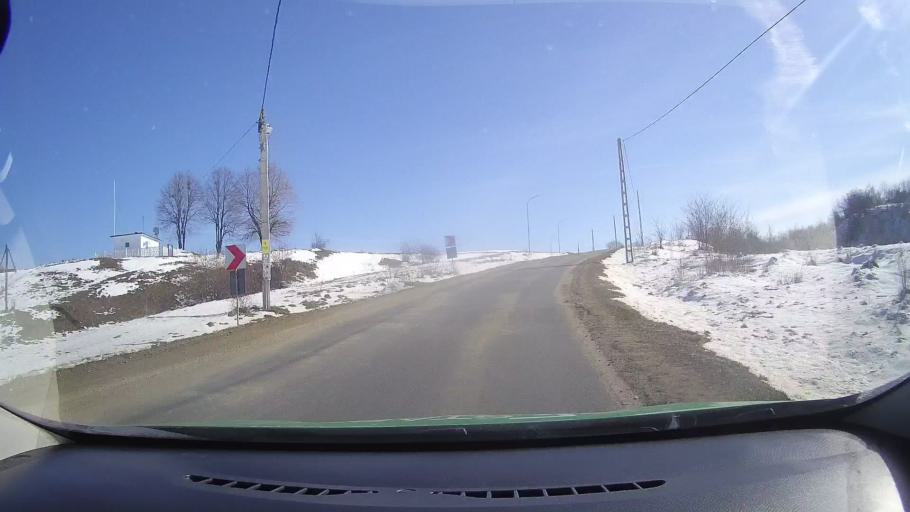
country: RO
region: Brasov
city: Ucea de Sus
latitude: 45.7544
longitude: 24.6872
